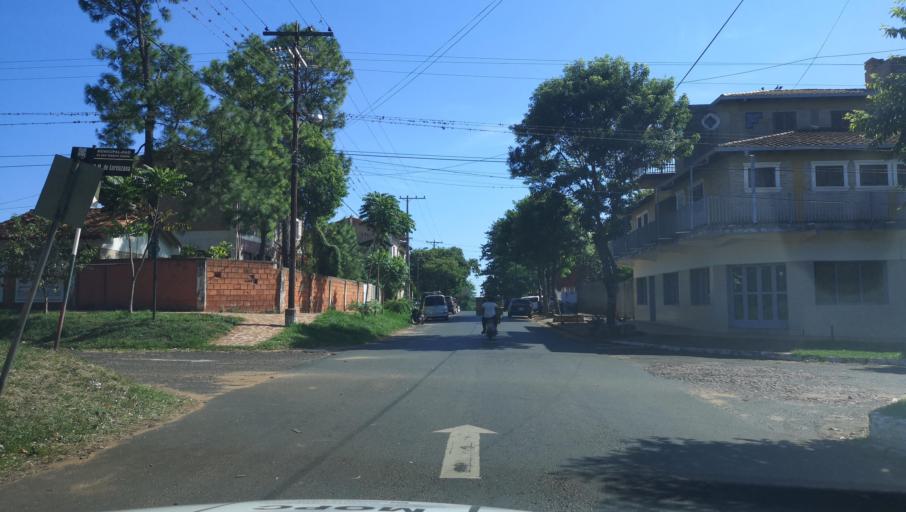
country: PY
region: Misiones
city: Santa Maria
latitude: -26.8904
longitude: -57.0221
